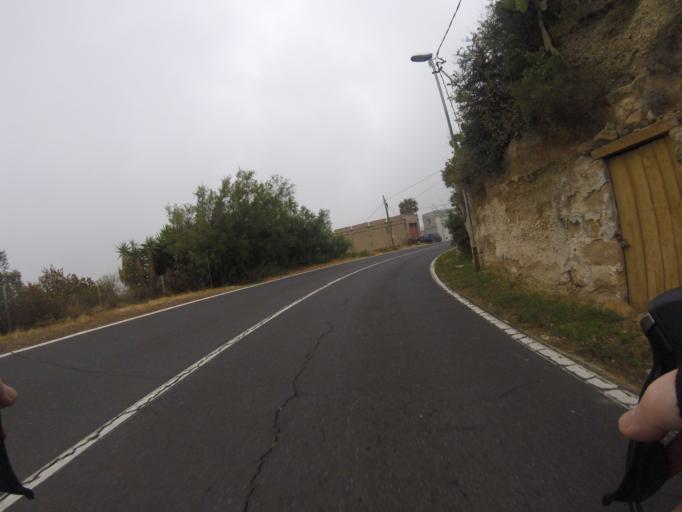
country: ES
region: Canary Islands
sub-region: Provincia de Santa Cruz de Tenerife
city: Guimar
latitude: 28.2817
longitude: -16.4067
